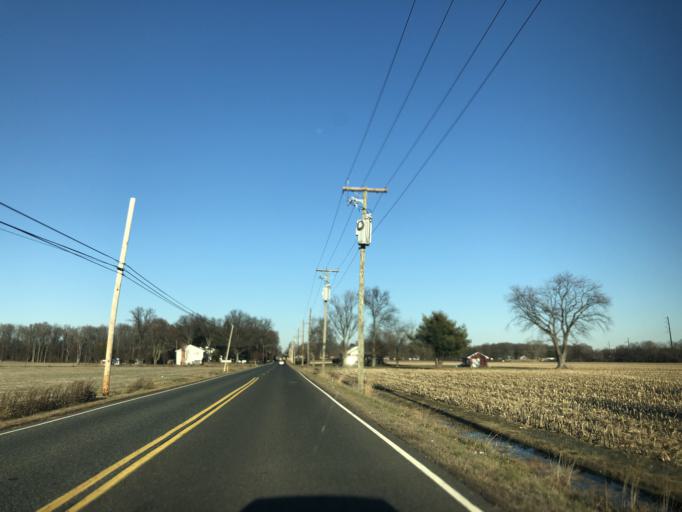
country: US
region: New Jersey
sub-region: Salem County
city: Carneys Point
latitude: 39.7078
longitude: -75.4552
